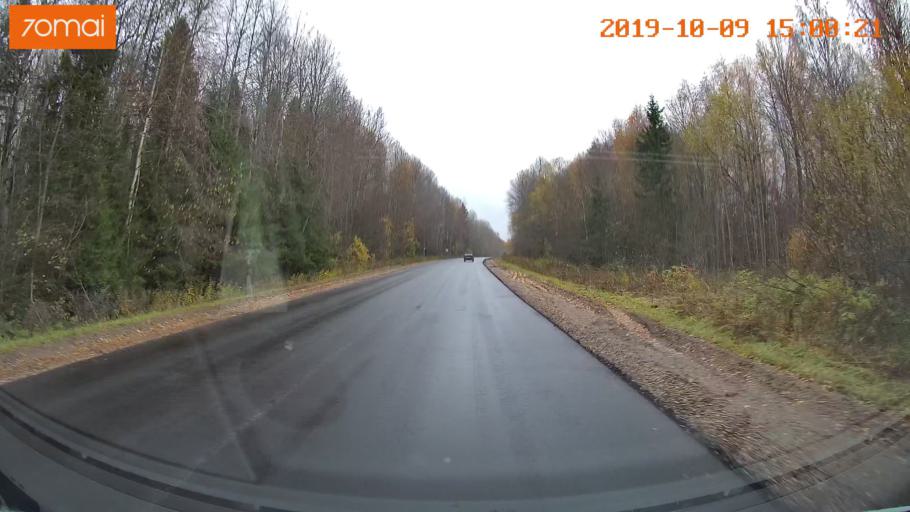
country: RU
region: Kostroma
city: Chistyye Bory
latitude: 58.3104
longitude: 41.6775
